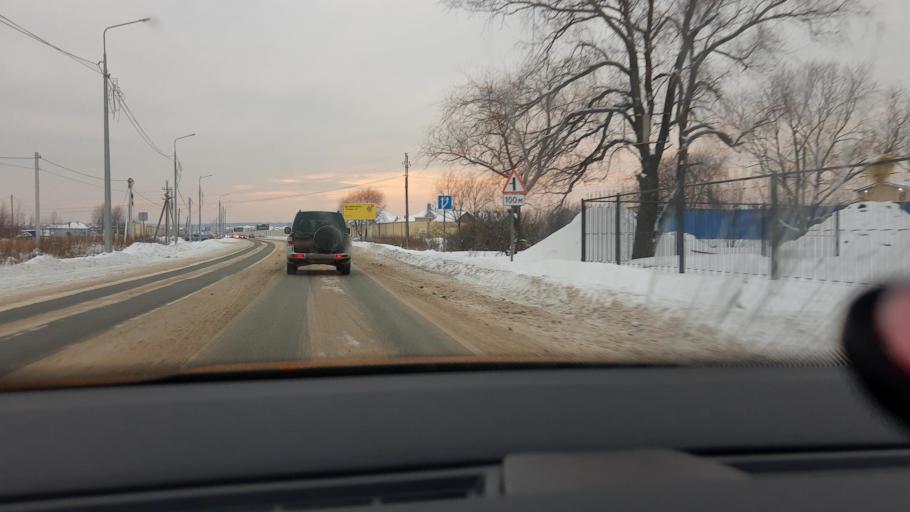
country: RU
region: Moskovskaya
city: Rozhdestveno
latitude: 55.8110
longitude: 37.0034
